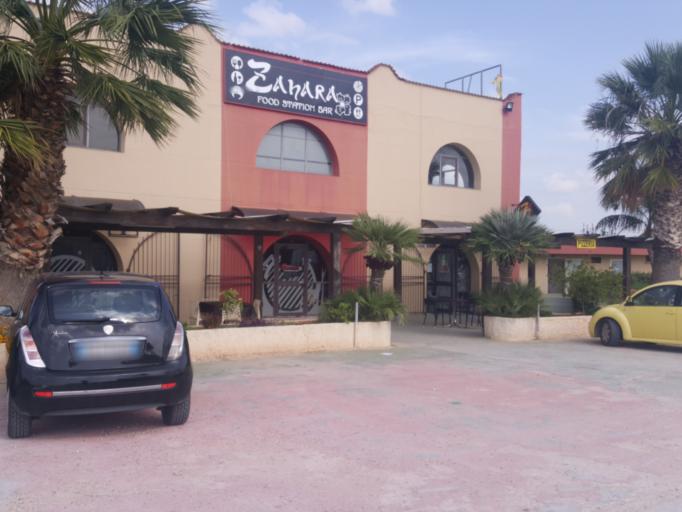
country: IT
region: Sicily
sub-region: Agrigento
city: Ribera
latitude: 37.4925
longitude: 13.2159
